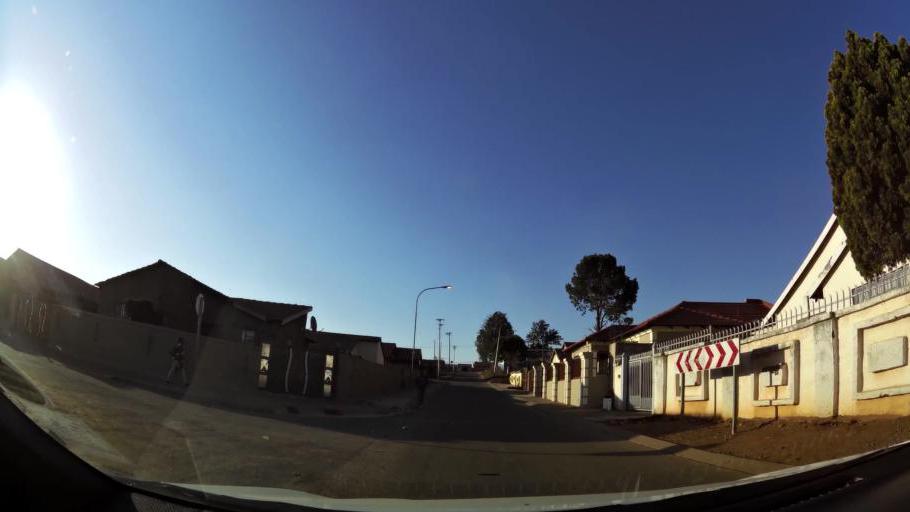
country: ZA
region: Gauteng
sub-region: City of Tshwane Metropolitan Municipality
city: Cullinan
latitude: -25.7271
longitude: 28.3896
